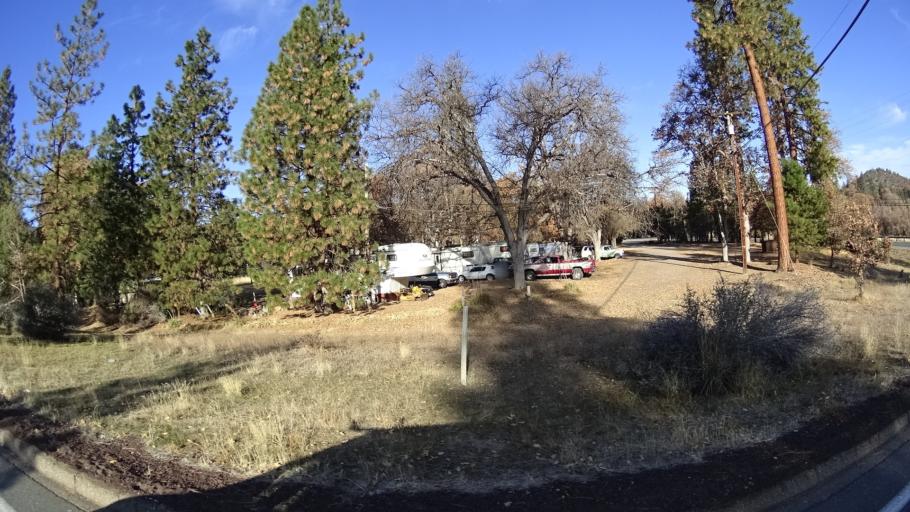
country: US
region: California
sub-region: Siskiyou County
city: Yreka
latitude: 41.6863
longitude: -122.6344
